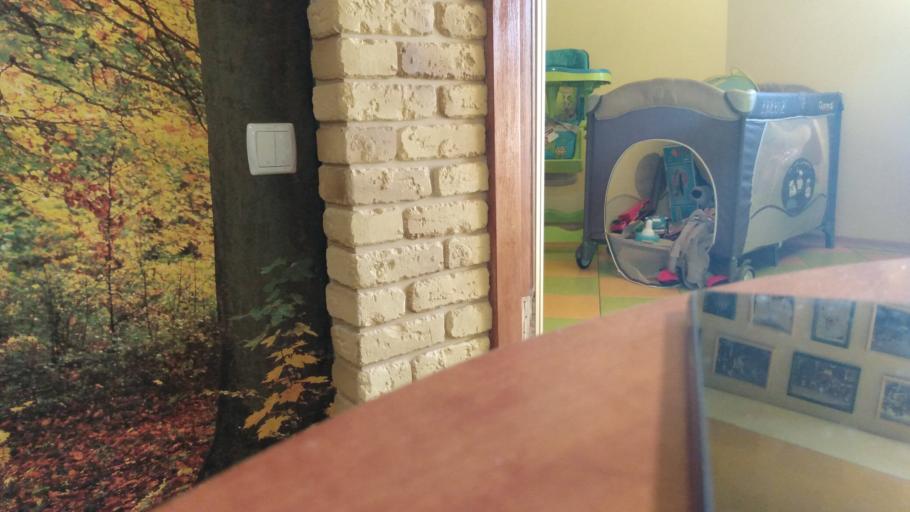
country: RU
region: Tverskaya
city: Bologoye
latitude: 57.8866
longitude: 34.2802
